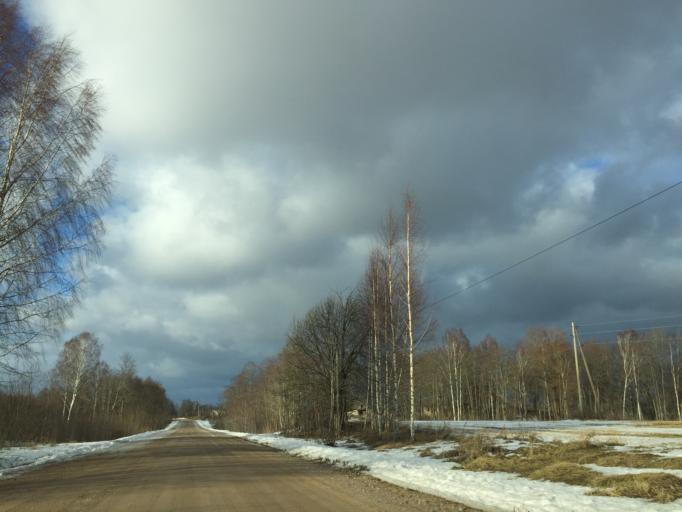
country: LV
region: Limbazu Rajons
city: Limbazi
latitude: 57.6191
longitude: 24.5773
